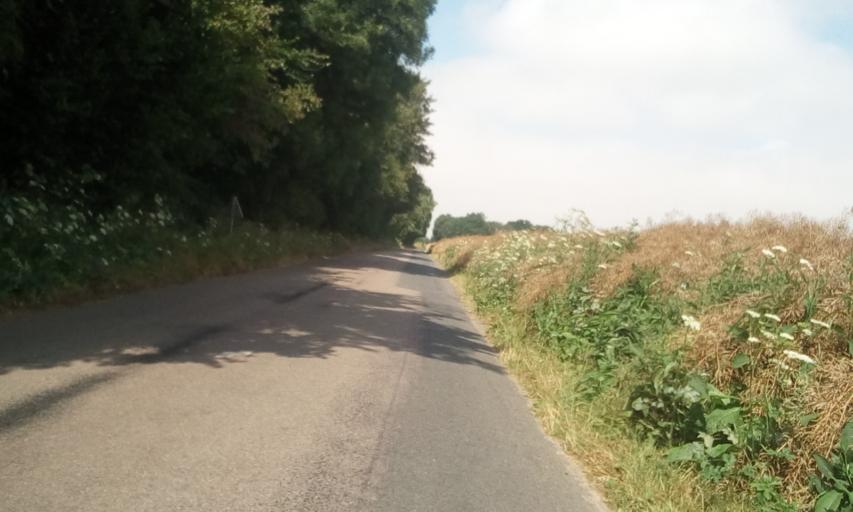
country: FR
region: Lower Normandy
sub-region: Departement du Calvados
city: Douvres-la-Delivrande
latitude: 49.2916
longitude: -0.4117
